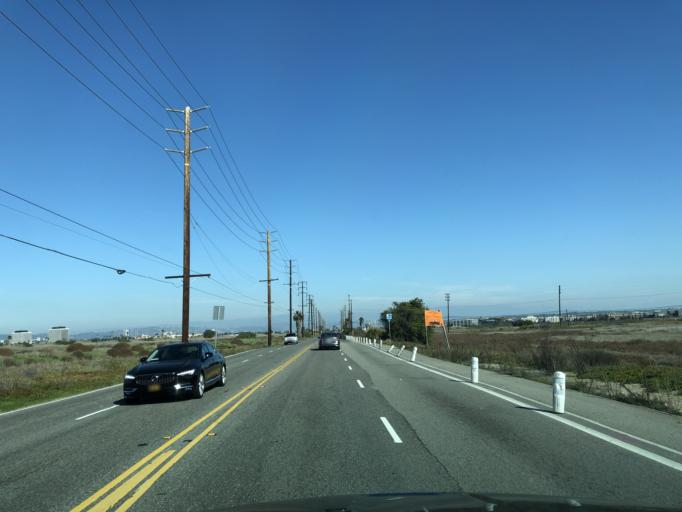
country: US
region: California
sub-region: Los Angeles County
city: Marina del Rey
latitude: 33.9634
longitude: -118.4434
